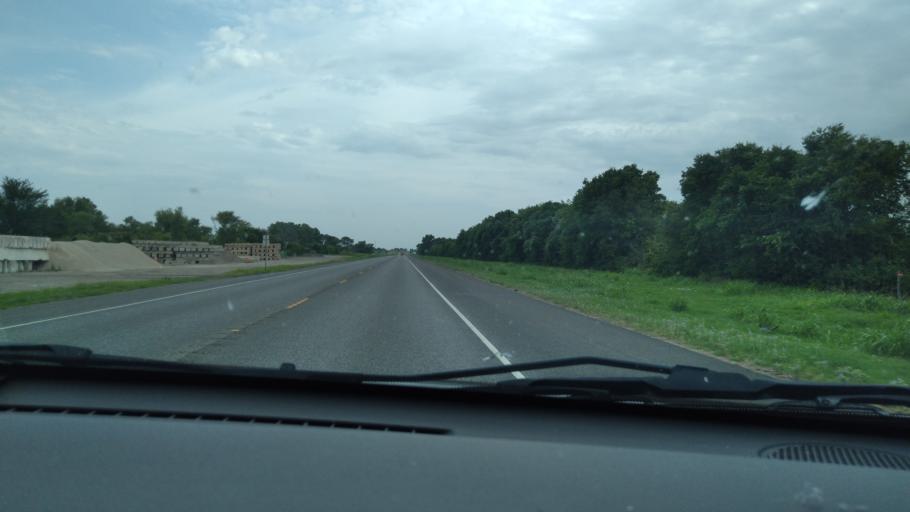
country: US
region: Texas
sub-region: McLennan County
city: Bellmead
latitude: 31.5604
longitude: -97.0680
